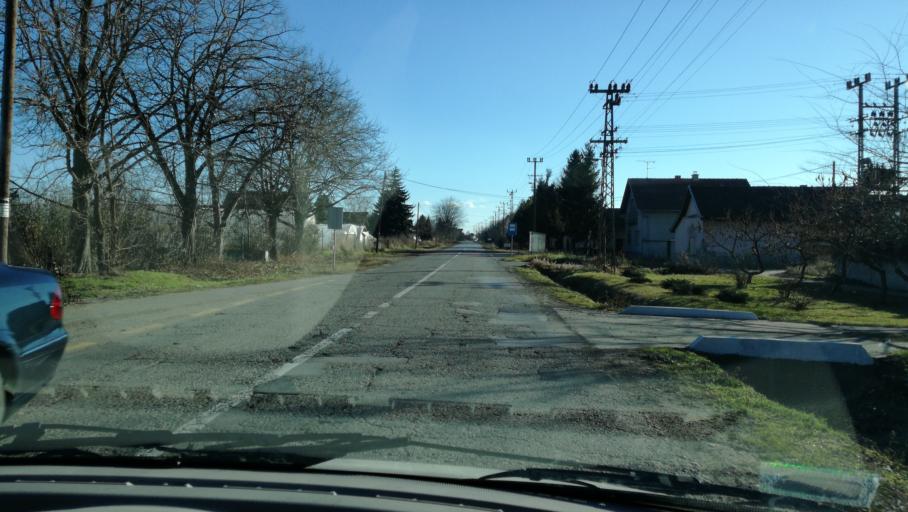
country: HU
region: Csongrad
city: Roszke
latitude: 46.1392
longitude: 19.9904
